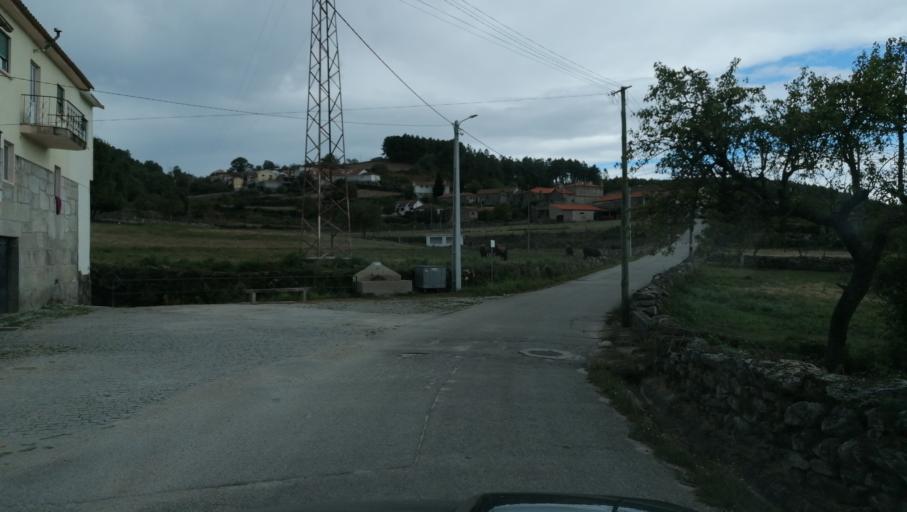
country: PT
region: Vila Real
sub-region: Vila Pouca de Aguiar
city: Vila Pouca de Aguiar
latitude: 41.5604
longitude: -7.6515
